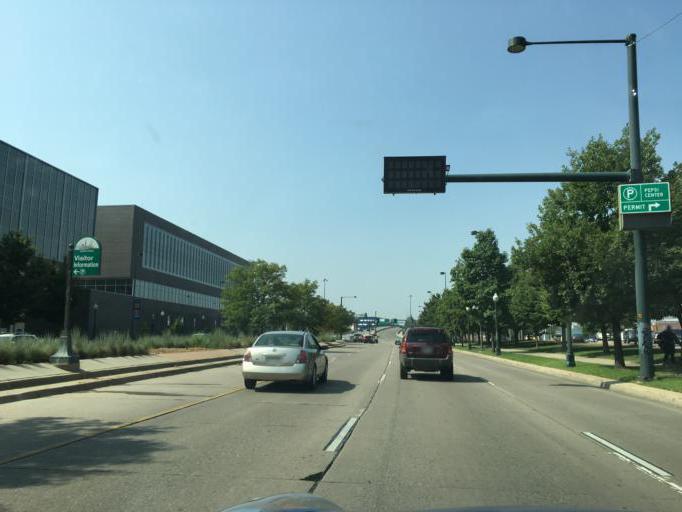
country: US
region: Colorado
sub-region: Denver County
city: Denver
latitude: 39.7462
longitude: -105.0082
